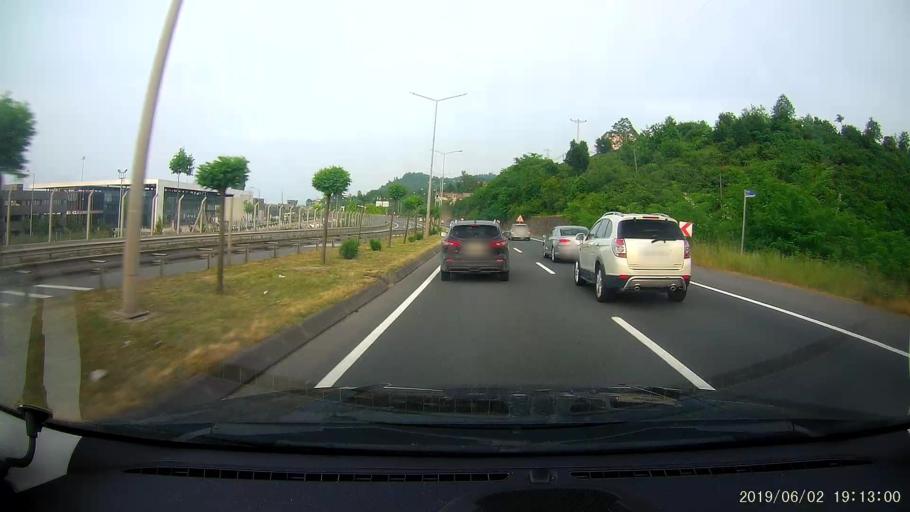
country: TR
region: Ordu
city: Gulyali
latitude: 40.9635
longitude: 38.0770
